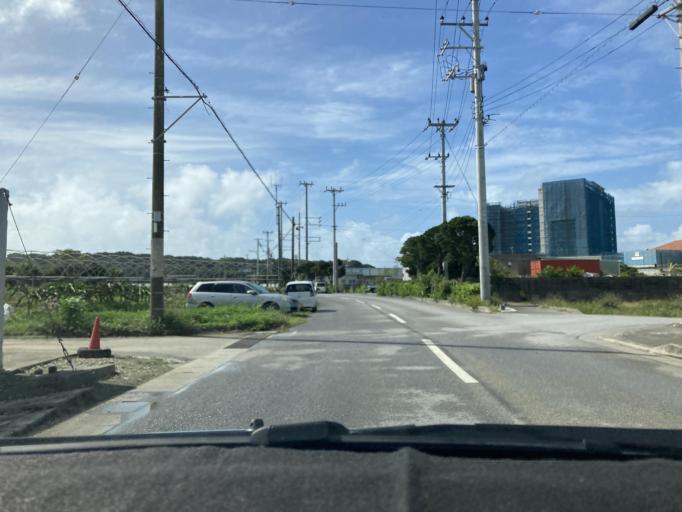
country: JP
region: Okinawa
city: Itoman
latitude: 26.1017
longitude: 127.6617
